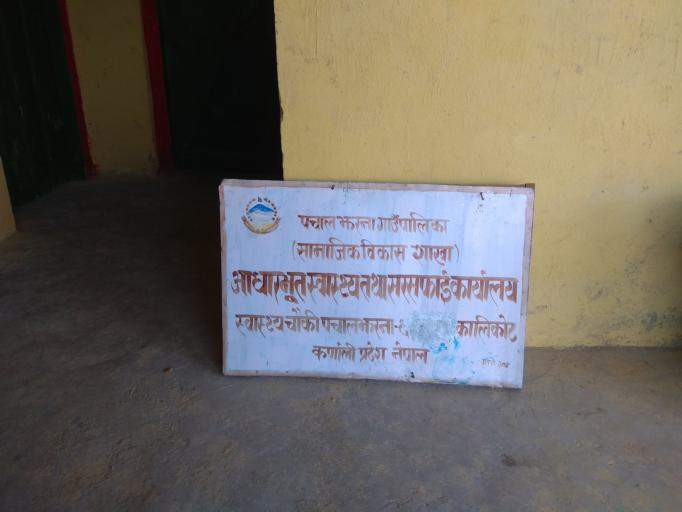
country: NP
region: Mid Western
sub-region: Karnali Zone
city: Jumla
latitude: 29.3182
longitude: 81.7245
